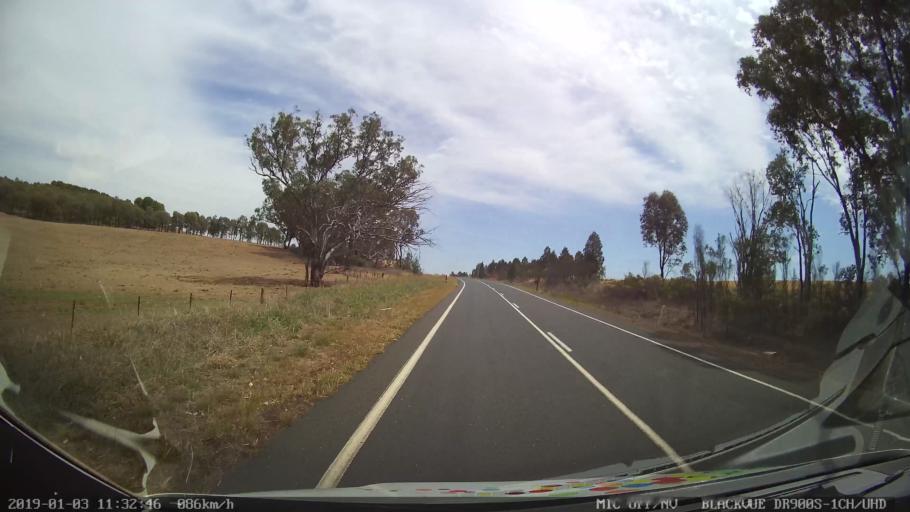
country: AU
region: New South Wales
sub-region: Weddin
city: Grenfell
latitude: -33.9541
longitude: 148.1766
